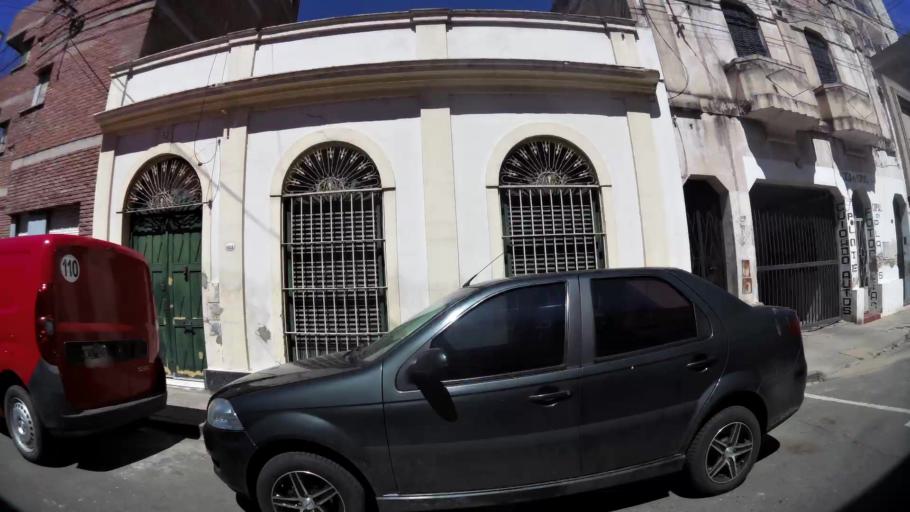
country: AR
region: Santa Fe
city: Santa Fe de la Vera Cruz
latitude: -31.6562
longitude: -60.7081
